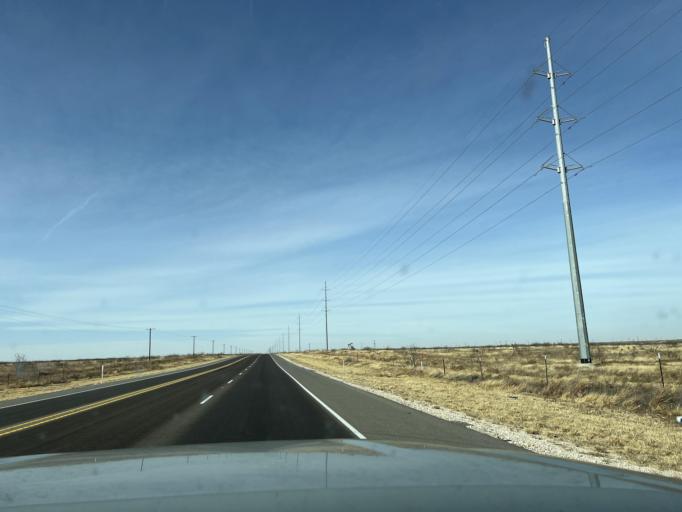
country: US
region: Texas
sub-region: Andrews County
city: Andrews
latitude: 32.3456
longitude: -102.7123
